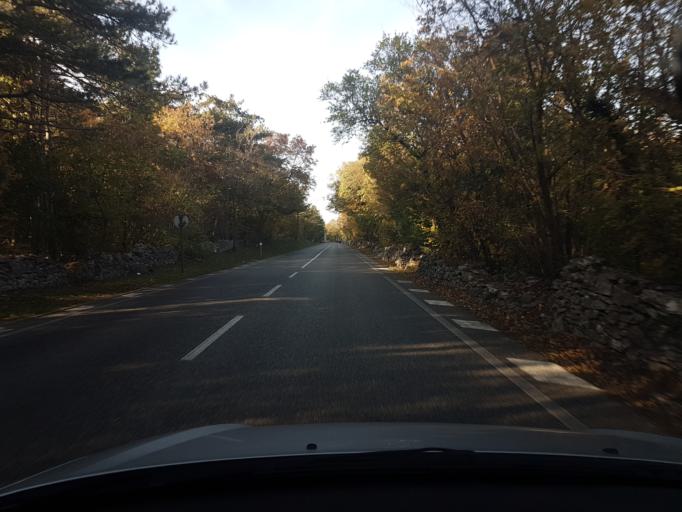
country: IT
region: Friuli Venezia Giulia
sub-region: Provincia di Trieste
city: Aurisina
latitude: 45.7433
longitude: 13.6813
